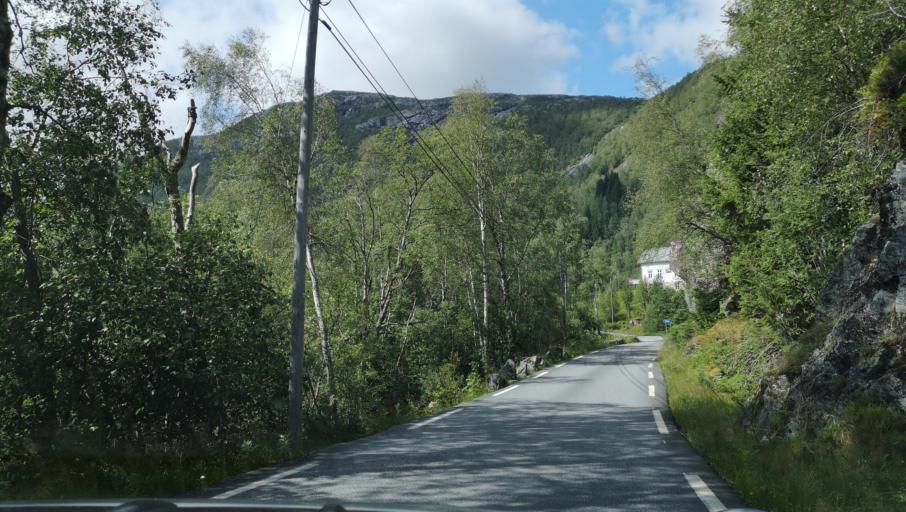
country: NO
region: Hordaland
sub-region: Modalen
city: Mo
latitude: 60.7830
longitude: 5.9431
